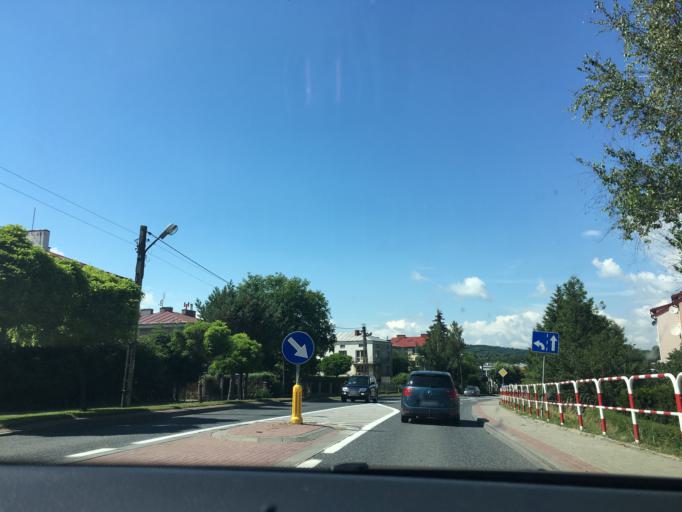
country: PL
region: Subcarpathian Voivodeship
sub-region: Powiat krosnienski
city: Dukla
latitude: 49.5504
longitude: 21.6832
